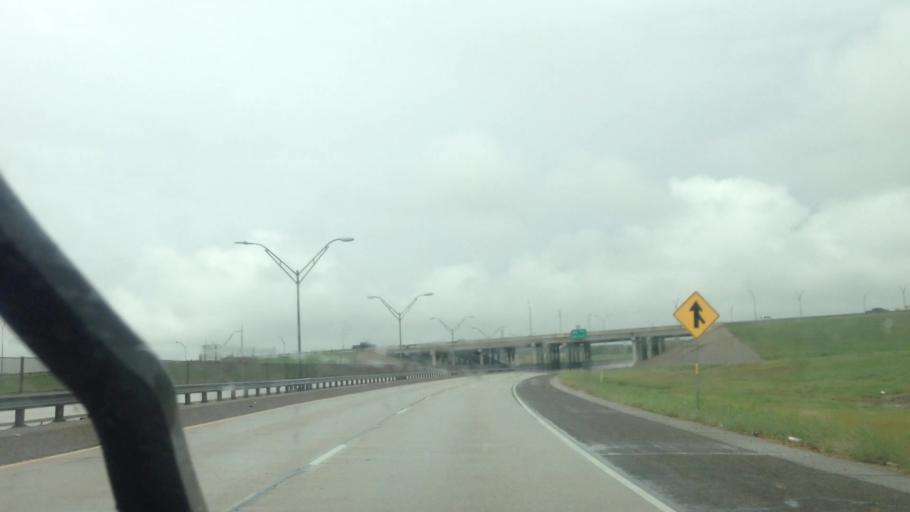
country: US
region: Texas
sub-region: Tarrant County
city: Saginaw
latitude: 32.8344
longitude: -97.3622
